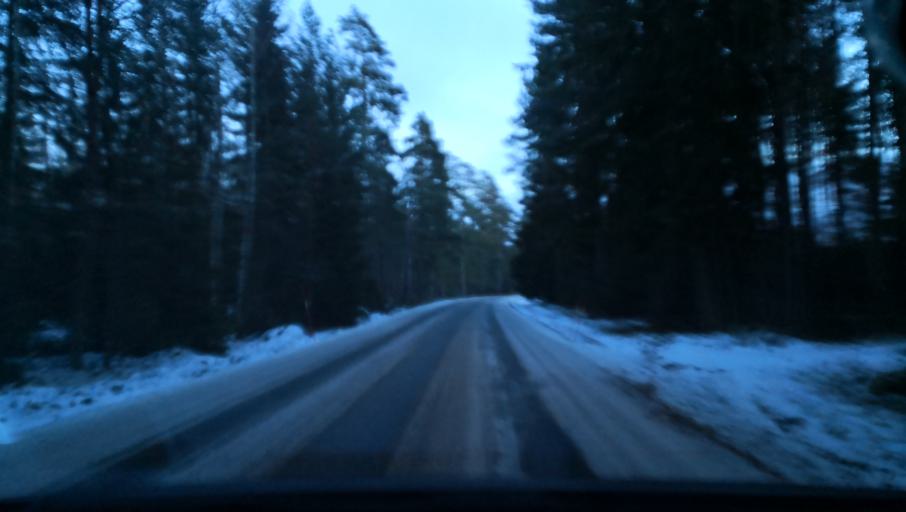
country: SE
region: Soedermanland
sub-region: Katrineholms Kommun
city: Katrineholm
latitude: 59.0801
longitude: 16.2464
